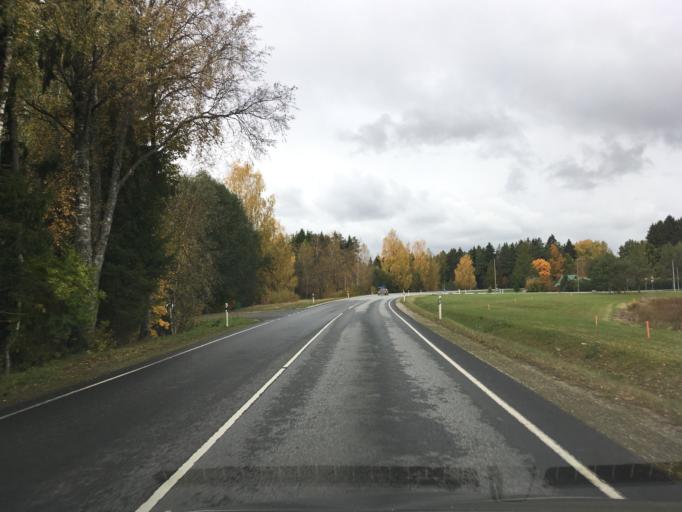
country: EE
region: Harju
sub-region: Anija vald
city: Kehra
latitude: 59.3111
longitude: 25.3461
